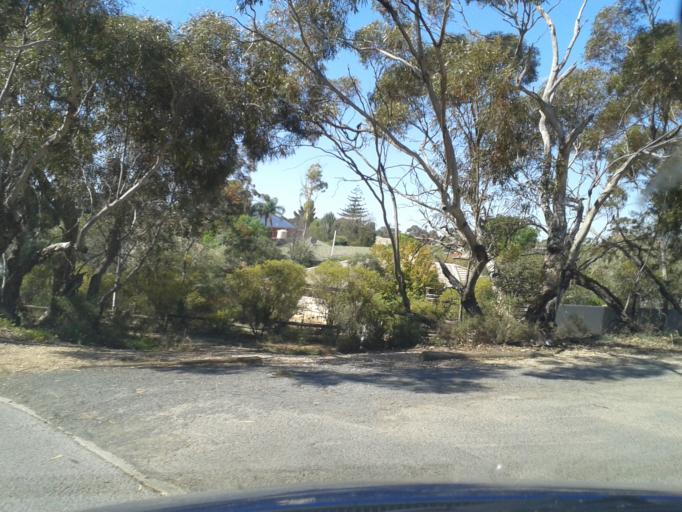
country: AU
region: South Australia
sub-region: Berri and Barmera
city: Berri
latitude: -34.2818
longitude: 140.6006
